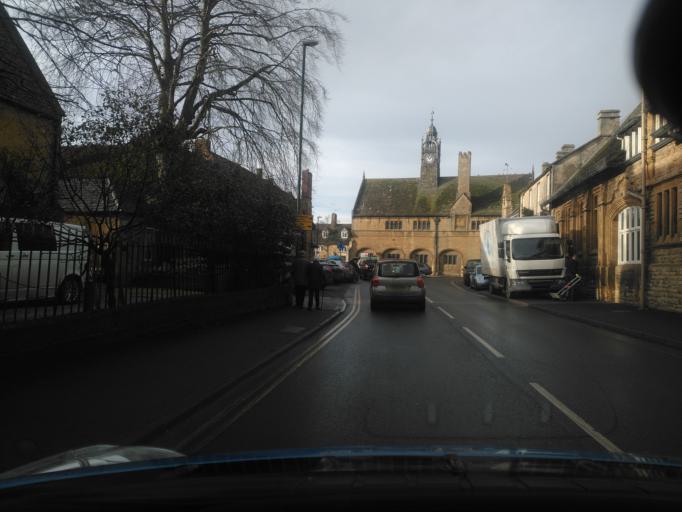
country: GB
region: England
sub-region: Gloucestershire
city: Moreton in Marsh
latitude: 51.9900
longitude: -1.7022
